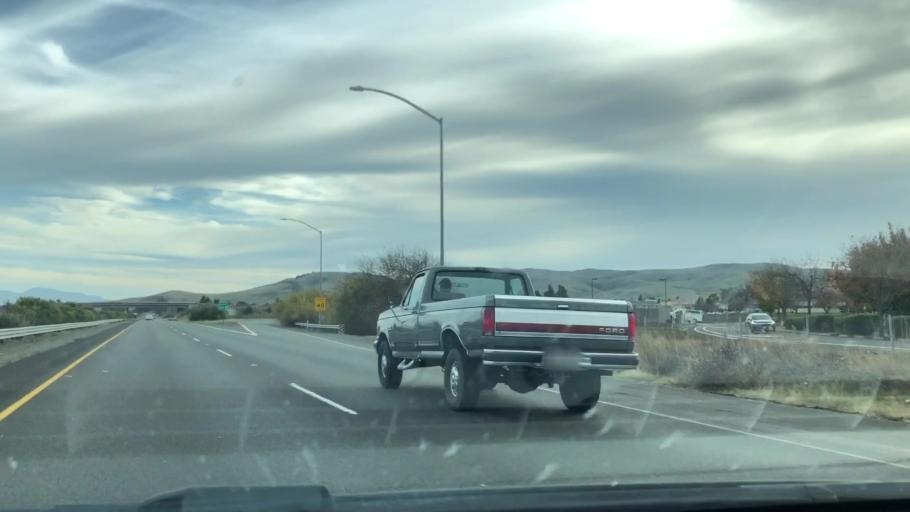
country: US
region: California
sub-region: Solano County
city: Green Valley
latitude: 38.1860
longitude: -122.1362
